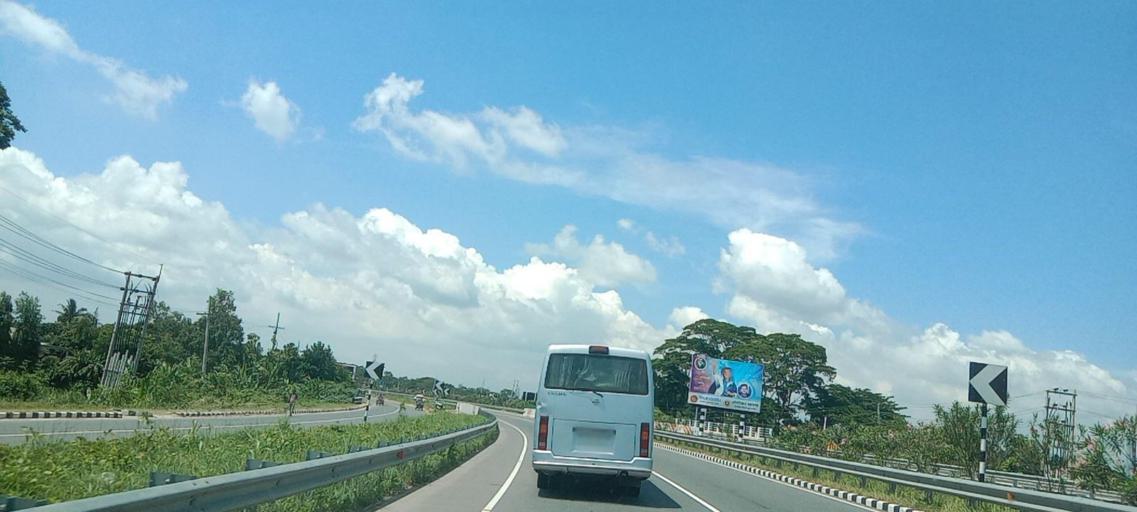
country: BD
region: Dhaka
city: Dohar
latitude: 23.5481
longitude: 90.2997
